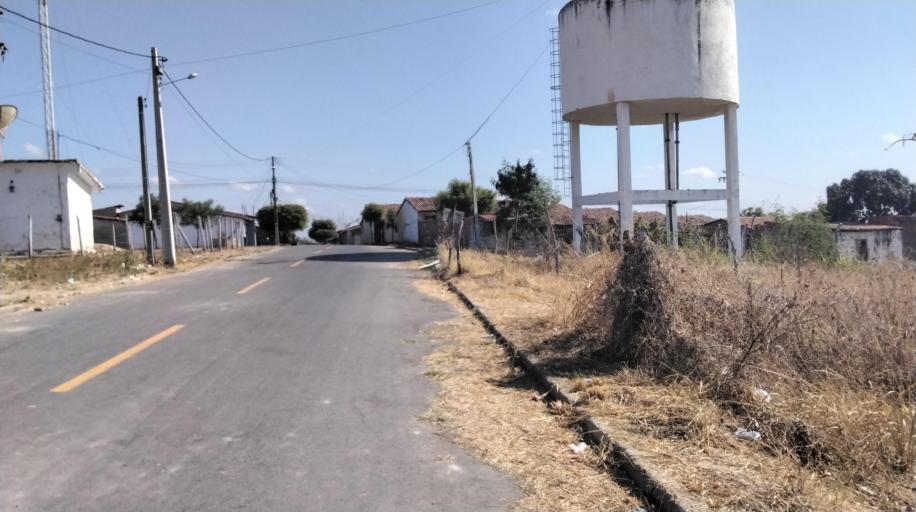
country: BR
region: Ceara
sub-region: Nova Russas
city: Nova Russas
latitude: -4.7058
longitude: -40.5734
